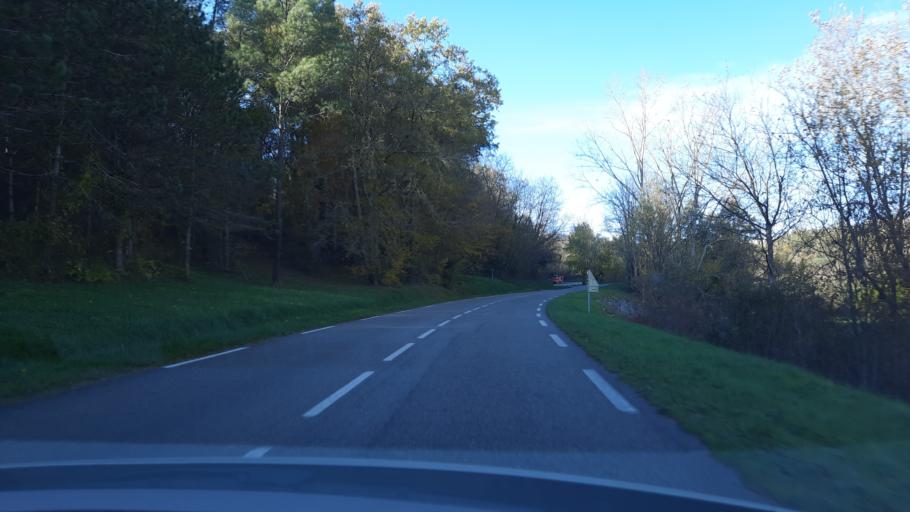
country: FR
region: Midi-Pyrenees
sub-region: Departement du Tarn-et-Garonne
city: Molieres
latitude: 44.1174
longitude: 1.3570
